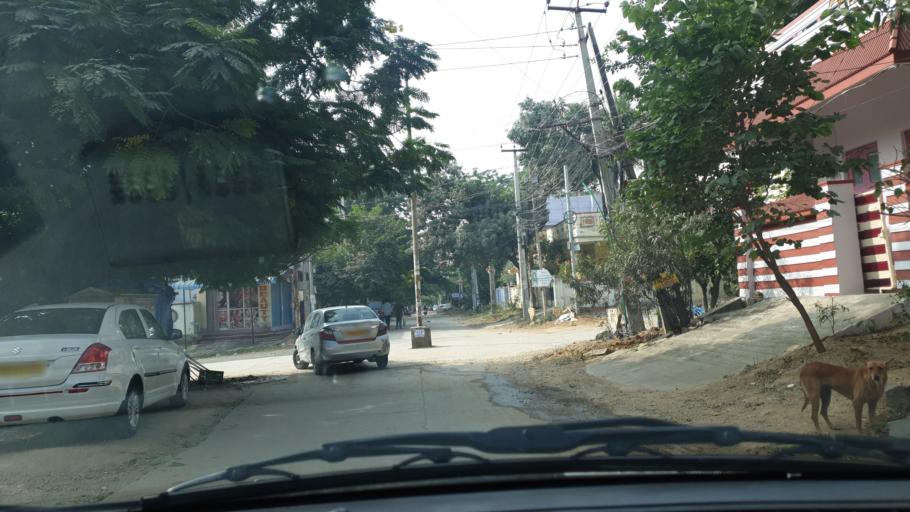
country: IN
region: Telangana
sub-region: Rangareddi
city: Kukatpalli
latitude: 17.4853
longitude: 78.4057
